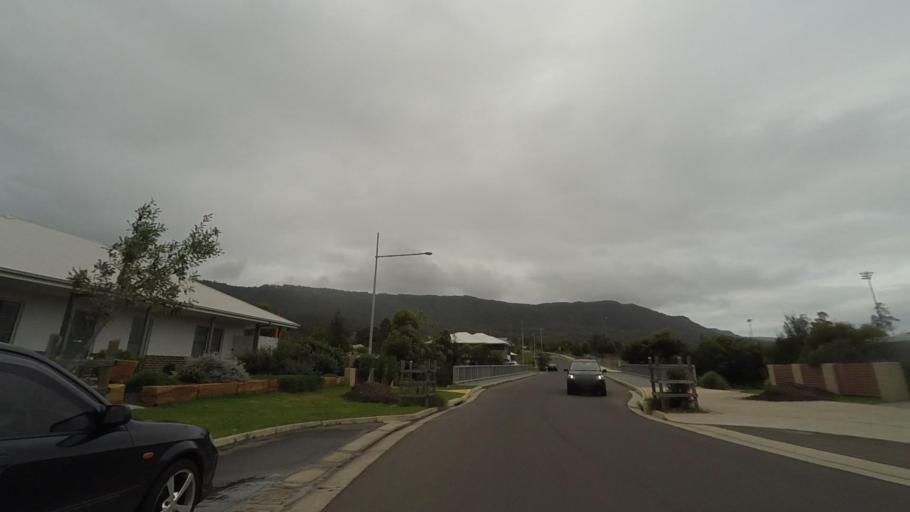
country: AU
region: New South Wales
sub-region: Wollongong
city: Bulli
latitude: -34.3216
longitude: 150.9178
